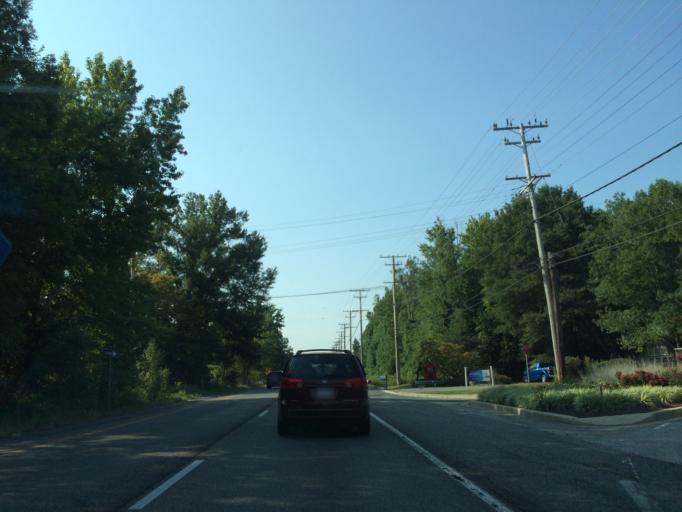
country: US
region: Maryland
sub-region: Prince George's County
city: Bowie
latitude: 38.9265
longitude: -76.7172
